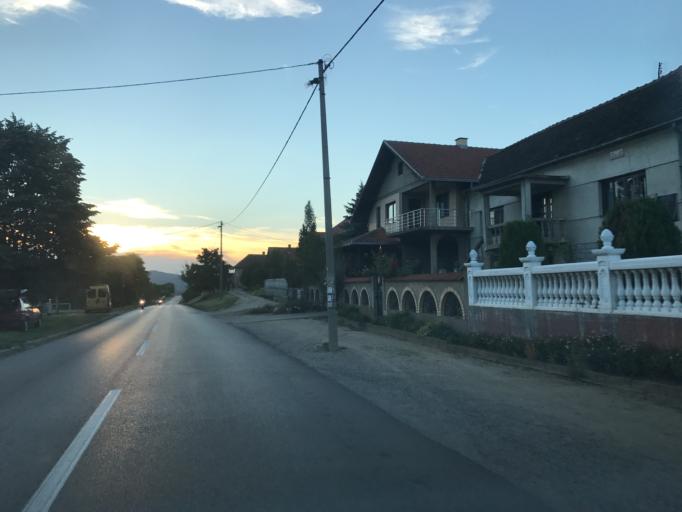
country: RS
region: Central Serbia
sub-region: Branicevski Okrug
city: Golubac
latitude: 44.6902
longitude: 21.5690
